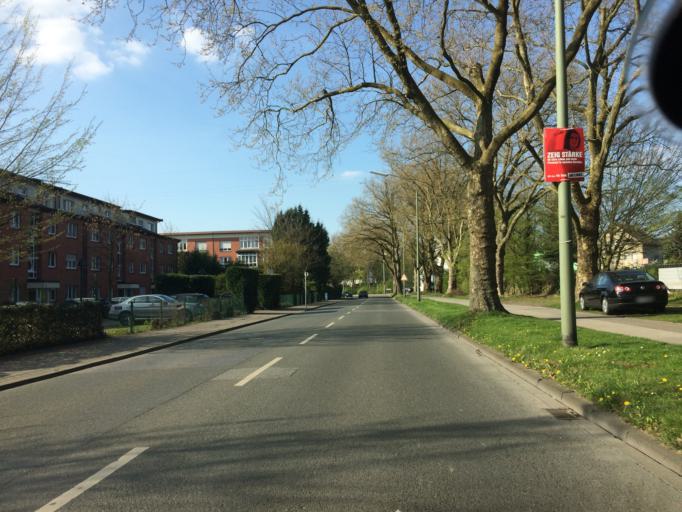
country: DE
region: North Rhine-Westphalia
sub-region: Regierungsbezirk Munster
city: Gelsenkirchen
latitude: 51.5229
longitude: 7.1058
